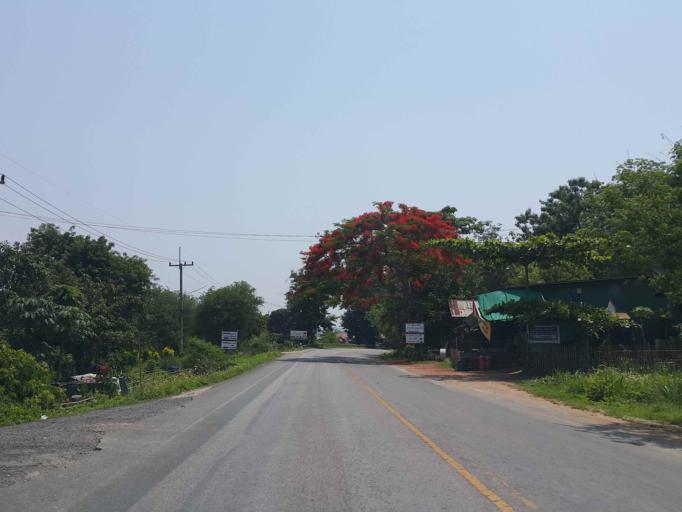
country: TH
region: Chiang Mai
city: Mae Taeng
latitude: 19.1162
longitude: 99.0053
